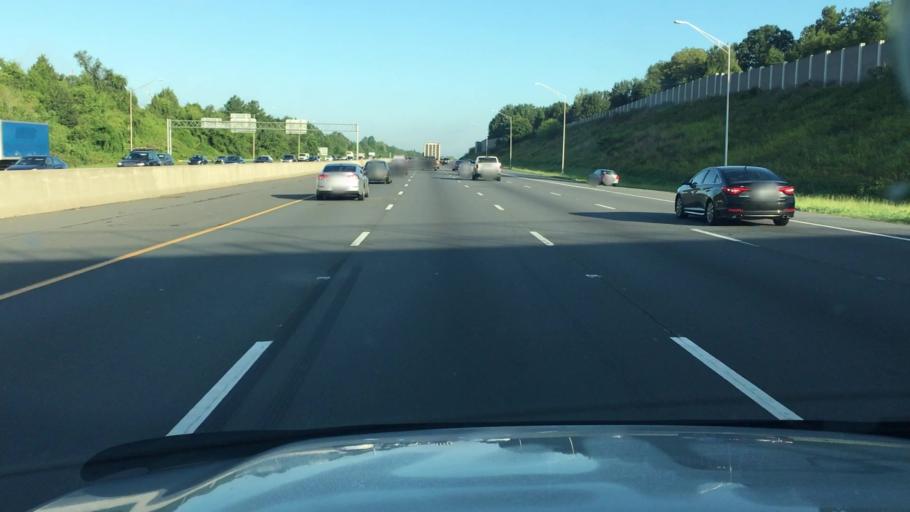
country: US
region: North Carolina
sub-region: Mecklenburg County
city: Pineville
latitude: 35.1027
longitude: -80.8829
